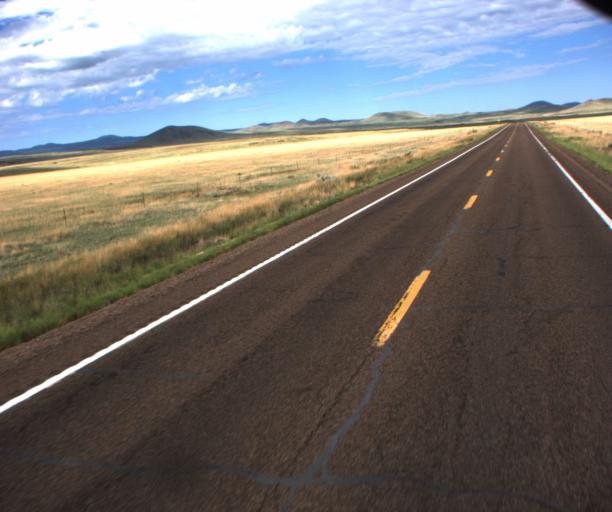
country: US
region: Arizona
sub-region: Apache County
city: Springerville
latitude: 34.1920
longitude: -109.3586
